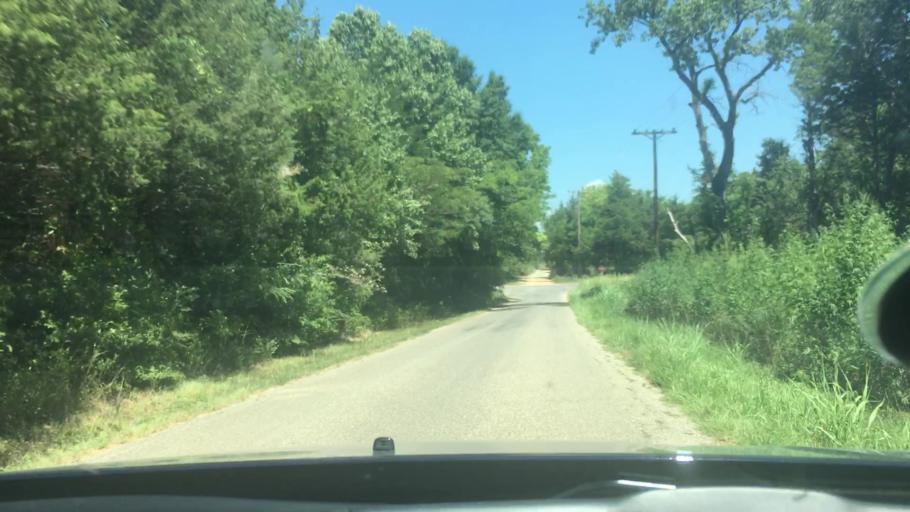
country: US
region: Oklahoma
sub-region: Bryan County
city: Durant
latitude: 33.9819
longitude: -96.2510
